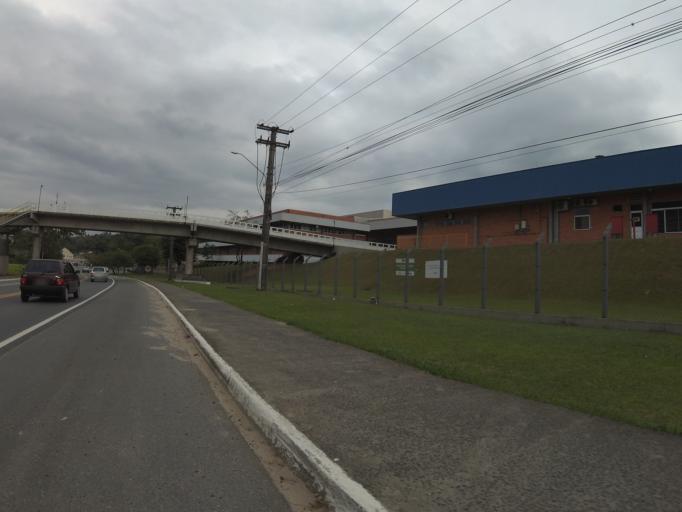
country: BR
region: Santa Catarina
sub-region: Indaial
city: Indaial
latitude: -26.8486
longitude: -49.1536
